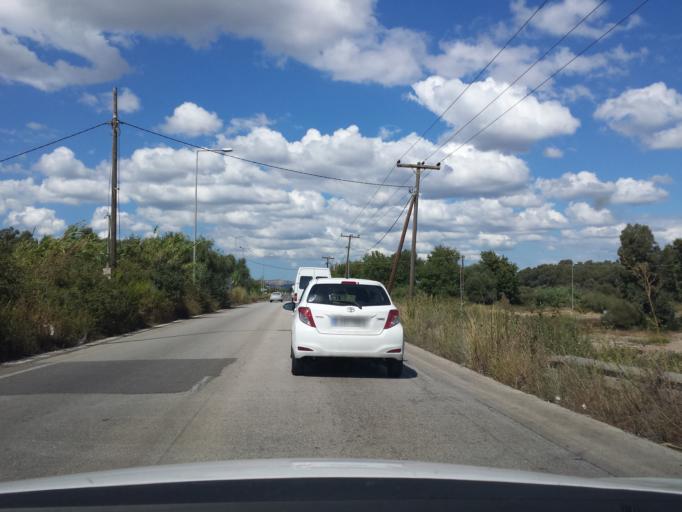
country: GR
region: West Greece
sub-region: Nomos Ileias
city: Epitalion
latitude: 37.6390
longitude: 21.4787
